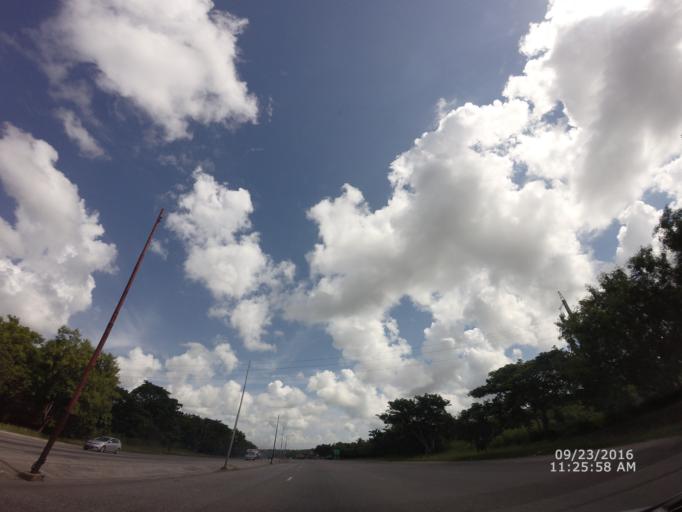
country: CU
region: La Habana
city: San Miguel del Padron
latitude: 23.0691
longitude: -82.2753
